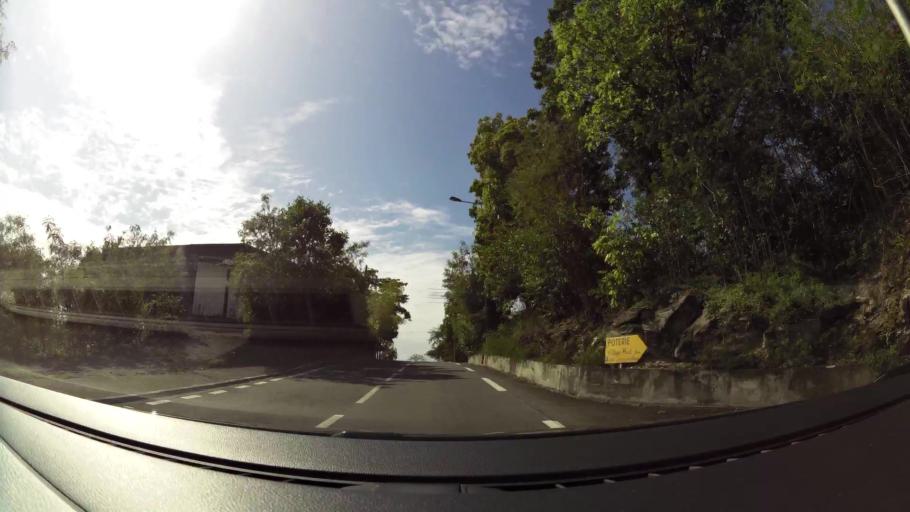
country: GP
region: Guadeloupe
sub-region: Guadeloupe
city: Bouillante
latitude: 16.0983
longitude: -61.7701
